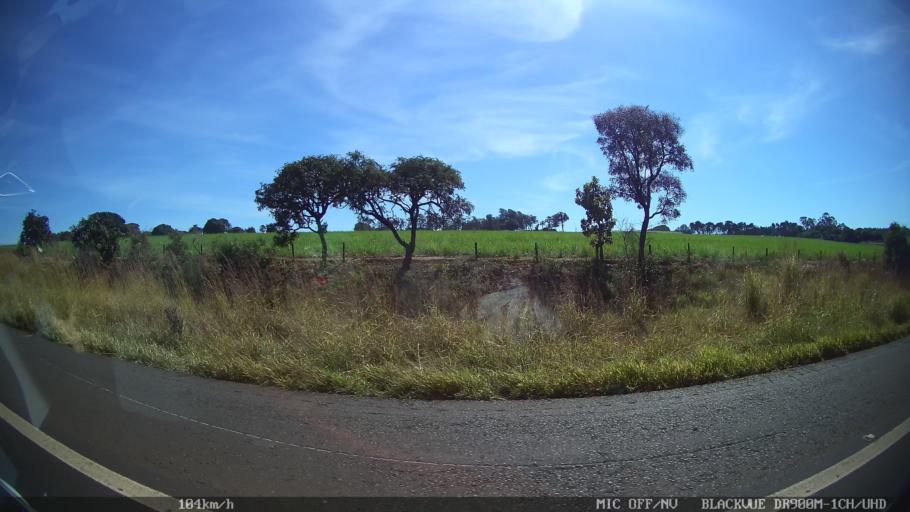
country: BR
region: Sao Paulo
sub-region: Franca
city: Franca
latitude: -20.5522
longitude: -47.4890
